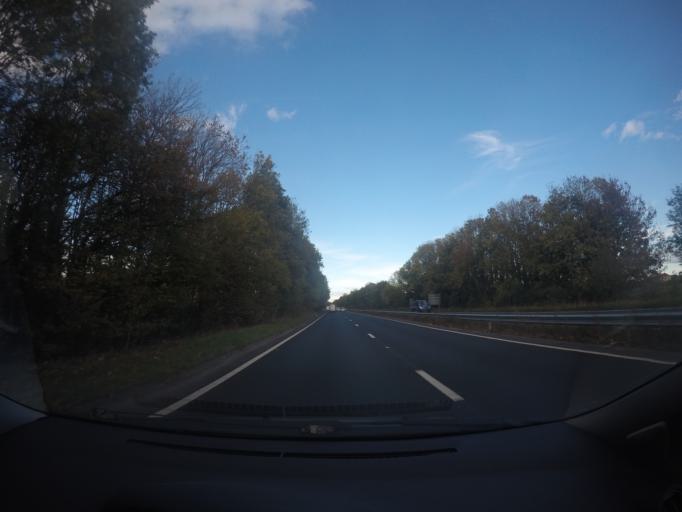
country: GB
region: England
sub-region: North Yorkshire
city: Tadcaster
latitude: 53.8818
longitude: -1.2538
